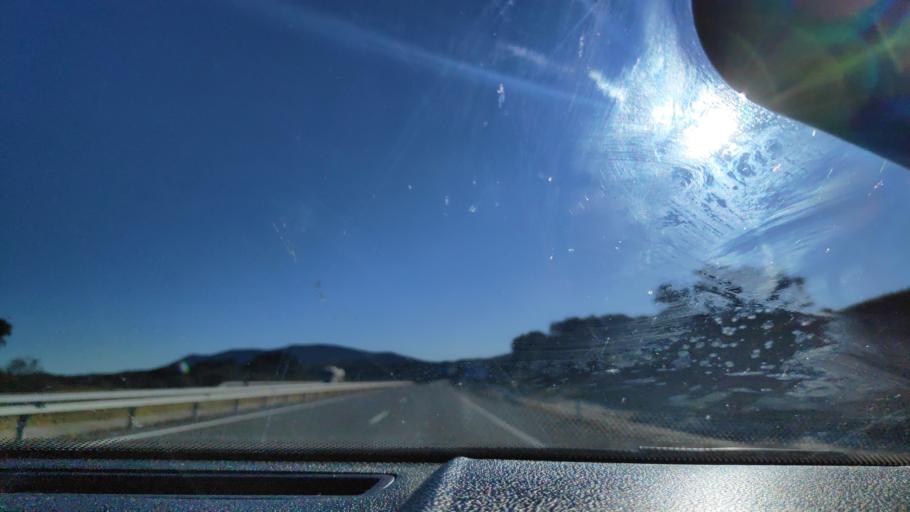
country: ES
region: Extremadura
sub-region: Provincia de Badajoz
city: Monesterio
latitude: 38.1144
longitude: -6.2695
